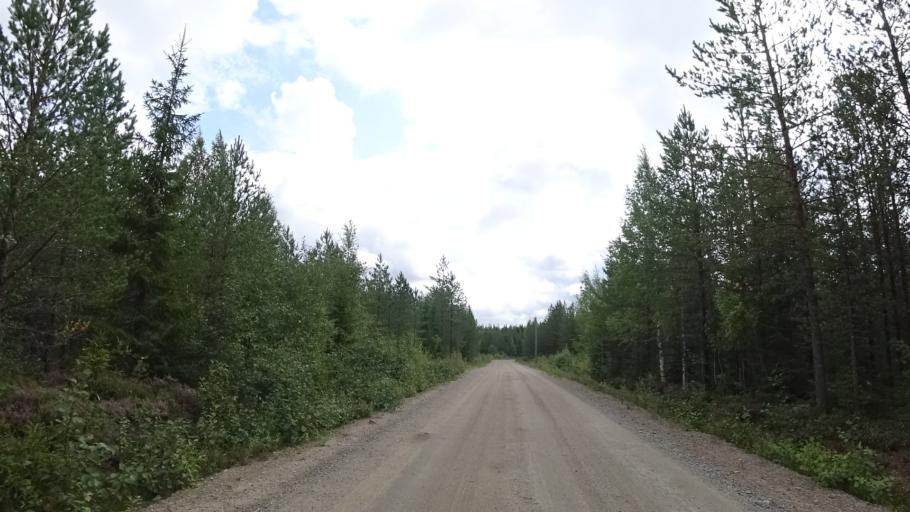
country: FI
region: North Karelia
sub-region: Joensuu
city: Ilomantsi
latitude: 62.9265
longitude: 31.3302
